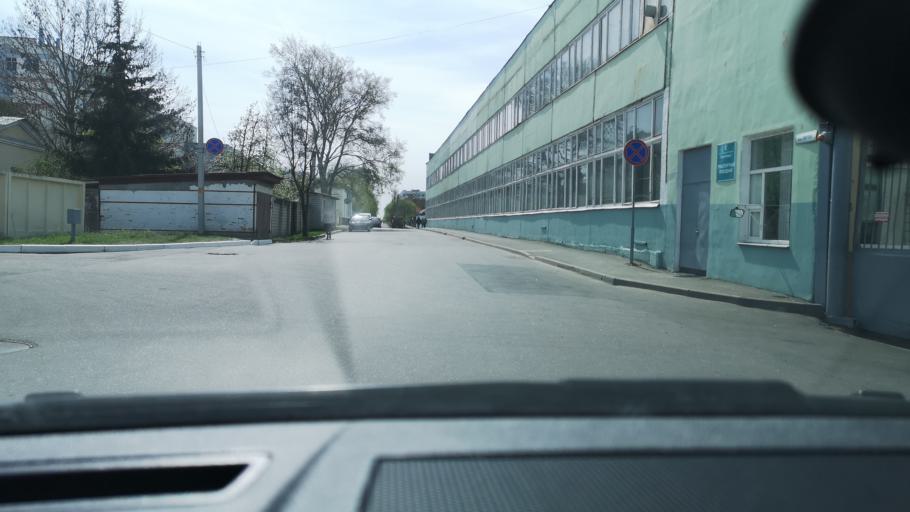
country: BY
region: Gomel
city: Gomel
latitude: 52.4212
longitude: 31.0094
